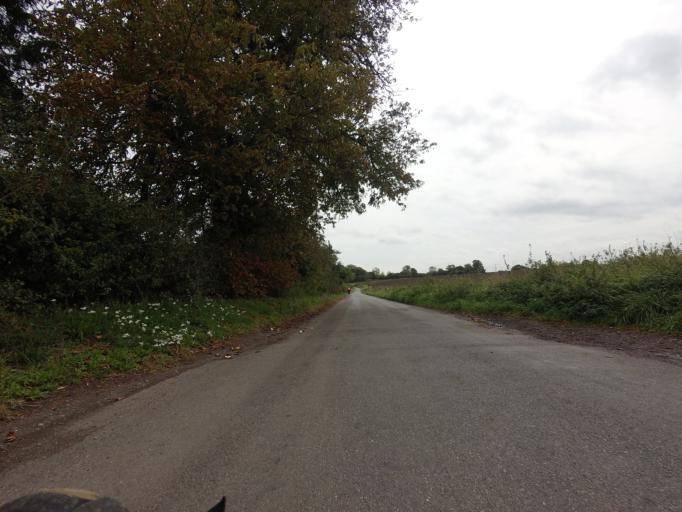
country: GB
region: England
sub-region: Hertfordshire
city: Reed
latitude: 51.9792
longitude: 0.0506
